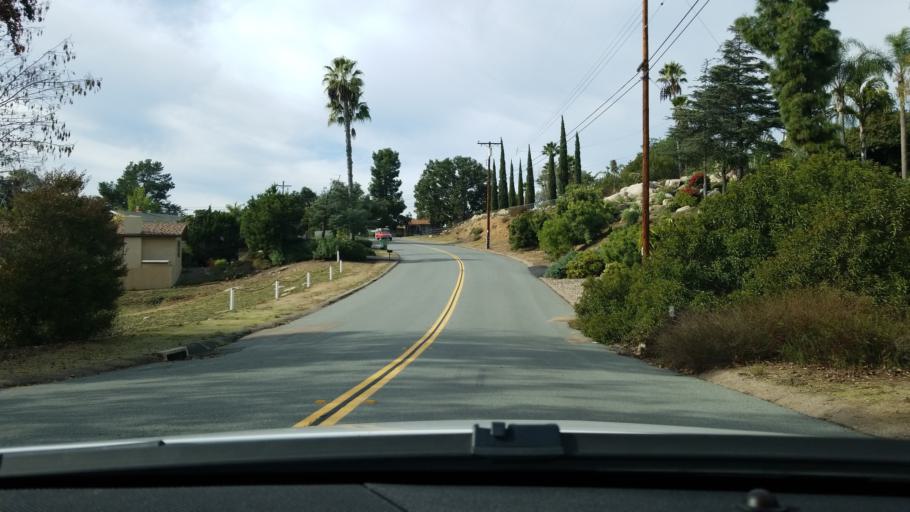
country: US
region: California
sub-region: San Diego County
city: Casa de Oro-Mount Helix
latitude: 32.7674
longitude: -116.9555
